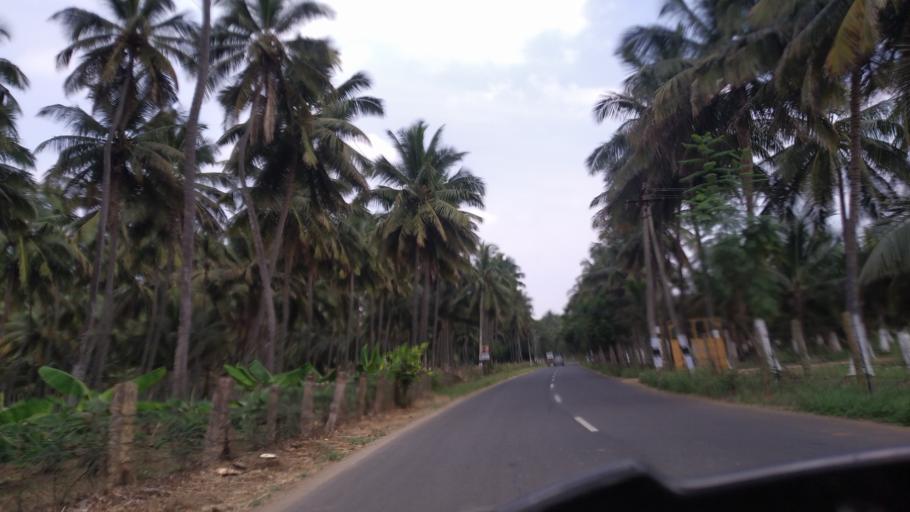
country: IN
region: Tamil Nadu
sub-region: Coimbatore
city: Perur
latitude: 10.9587
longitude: 76.7513
